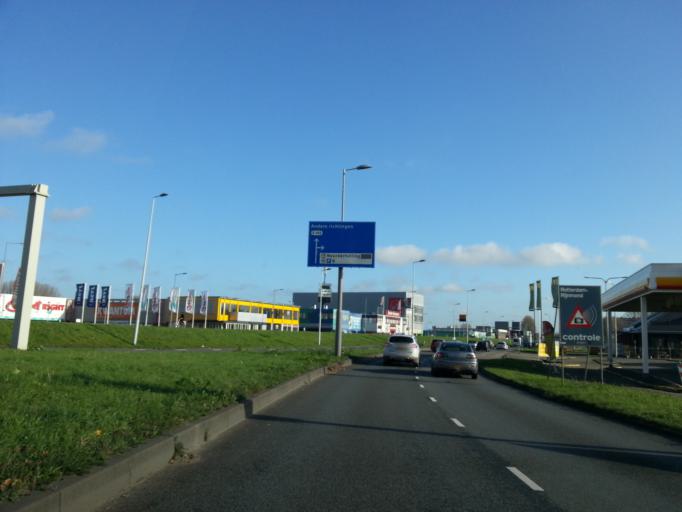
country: NL
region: South Holland
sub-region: Gemeente Rotterdam
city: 's-Gravenland
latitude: 51.8947
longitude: 4.5300
